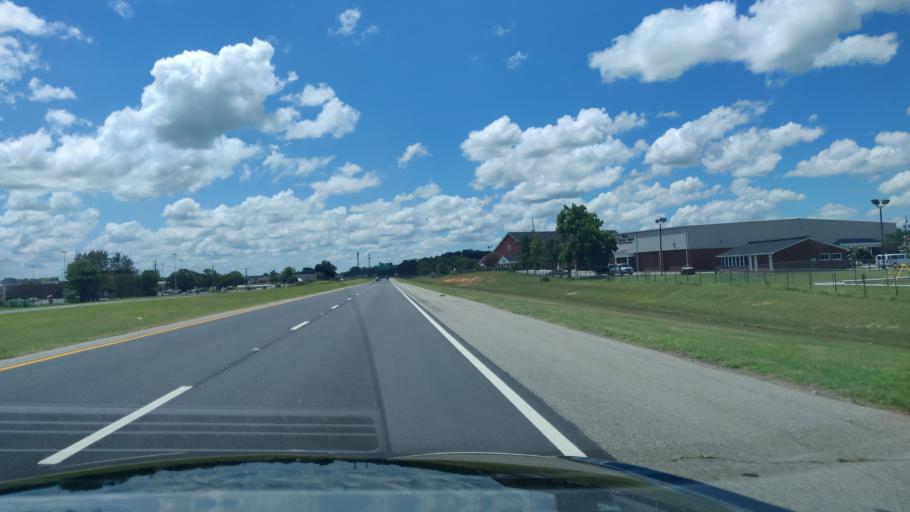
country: US
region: Georgia
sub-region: Dougherty County
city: Albany
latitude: 31.6201
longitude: -84.2130
